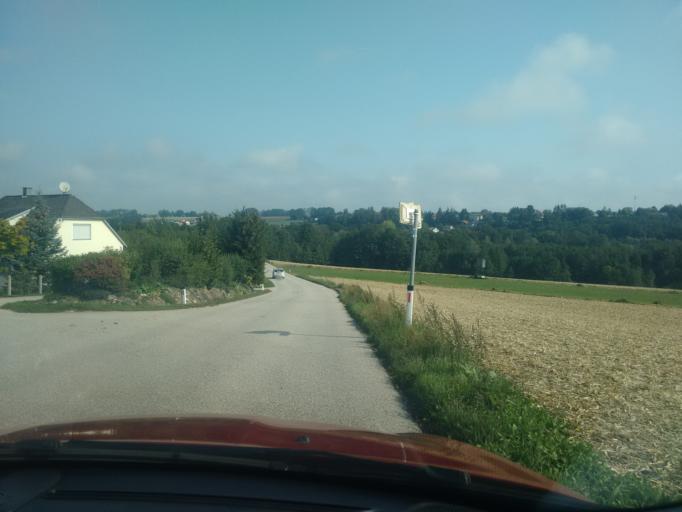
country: AT
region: Upper Austria
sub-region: Wels-Land
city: Steinhaus
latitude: 48.1175
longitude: 14.0082
